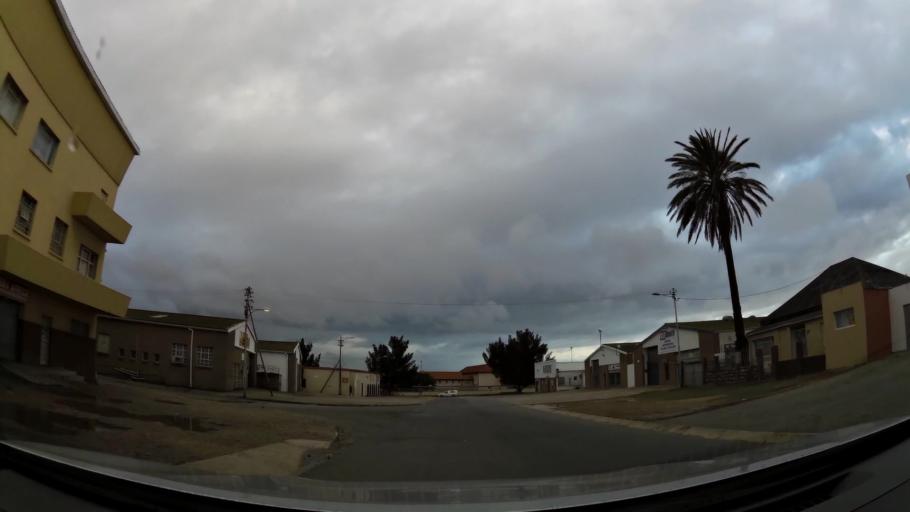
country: ZA
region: Eastern Cape
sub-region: Nelson Mandela Bay Metropolitan Municipality
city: Port Elizabeth
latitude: -33.9213
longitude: 25.5933
